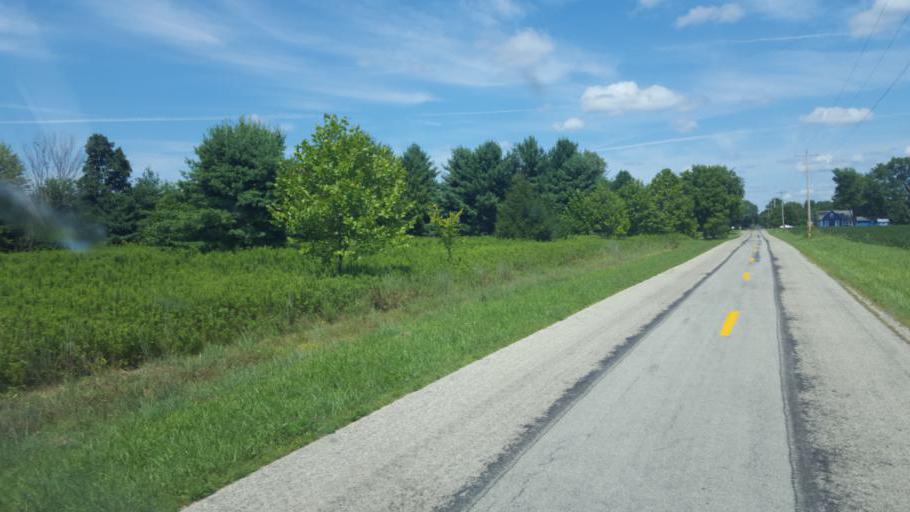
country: US
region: Ohio
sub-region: Delaware County
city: Sunbury
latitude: 40.3008
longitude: -82.8066
